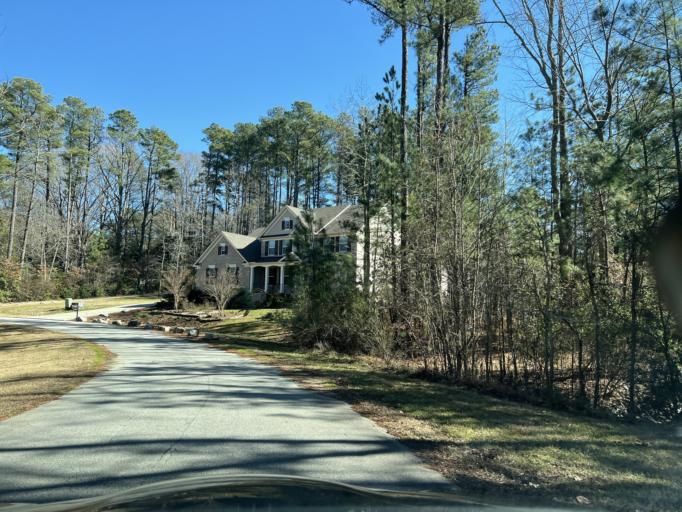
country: US
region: North Carolina
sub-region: Wake County
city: West Raleigh
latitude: 35.9006
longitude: -78.6127
